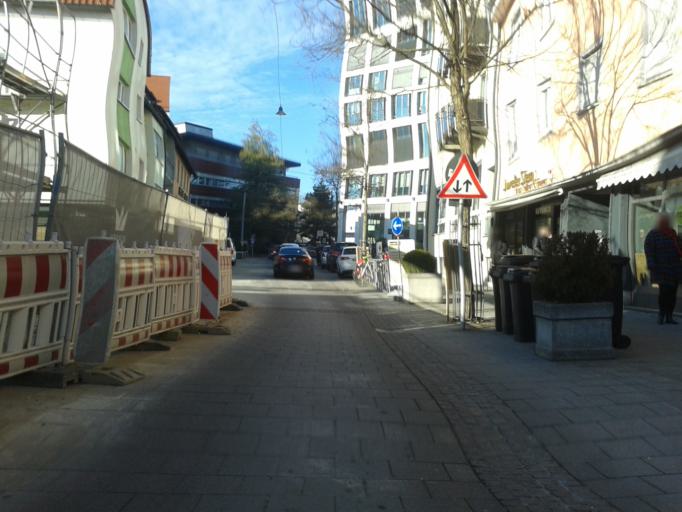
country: DE
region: Baden-Wuerttemberg
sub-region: Tuebingen Region
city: Ulm
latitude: 48.4003
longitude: 9.9886
